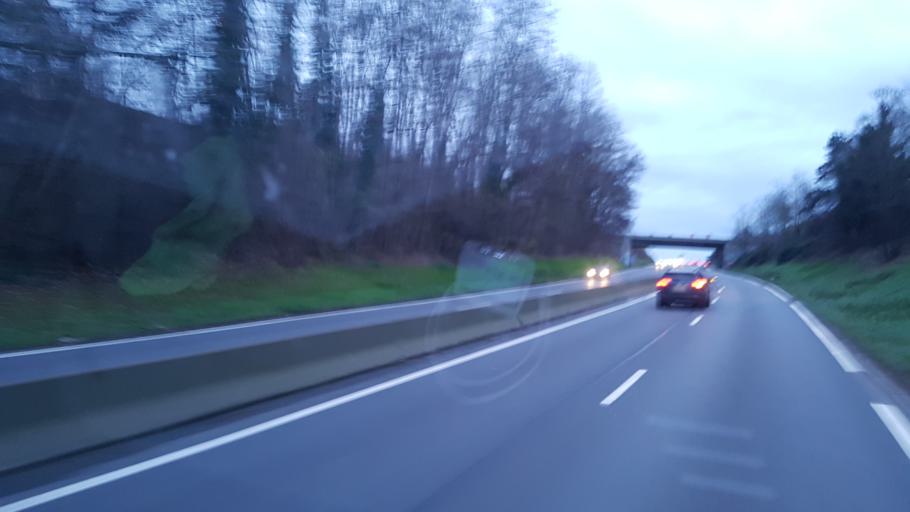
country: FR
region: Ile-de-France
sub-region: Departement de l'Essonne
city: Egly
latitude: 48.5848
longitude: 2.2337
